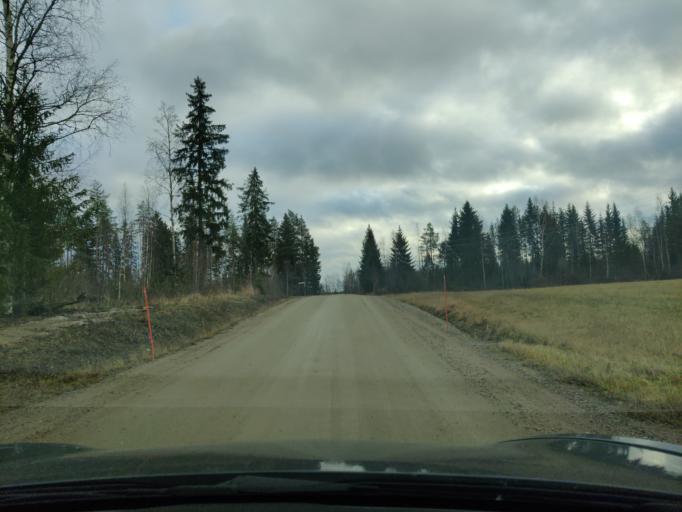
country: FI
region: Northern Savo
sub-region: Ylae-Savo
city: Kiuruvesi
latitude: 63.6385
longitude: 26.6450
